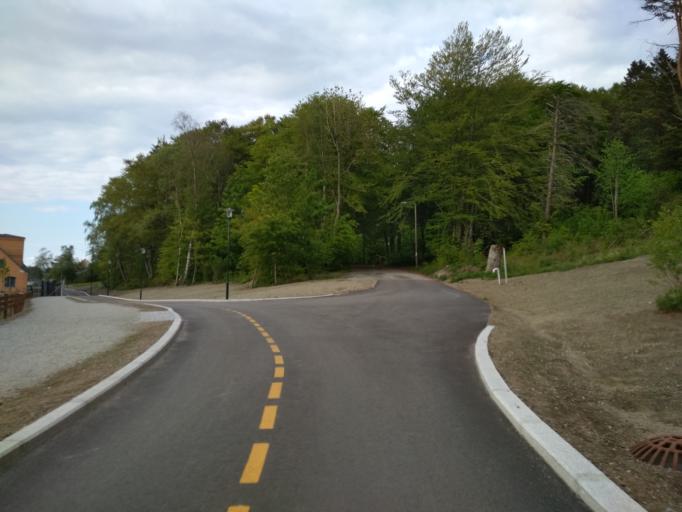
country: NO
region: Rogaland
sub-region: Stavanger
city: Stavanger
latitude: 58.9567
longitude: 5.7238
